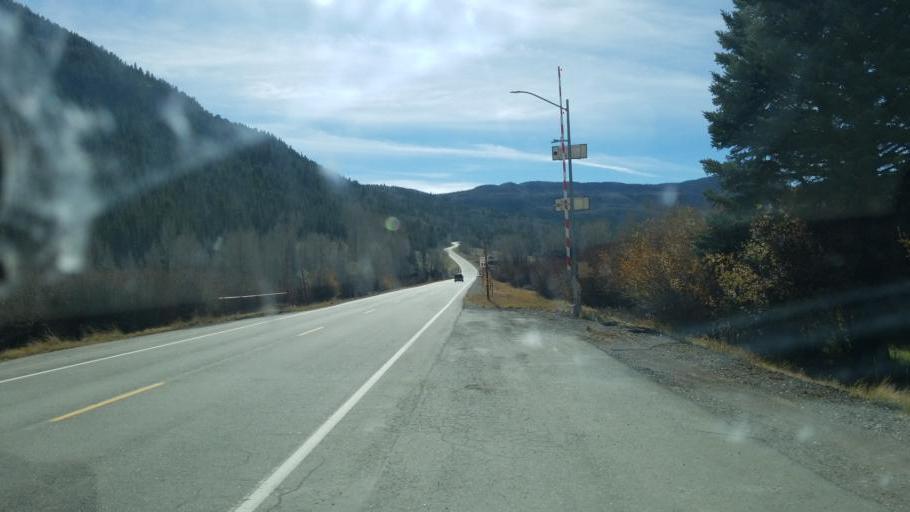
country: US
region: New Mexico
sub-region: Rio Arriba County
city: Chama
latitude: 37.1305
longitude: -106.3551
